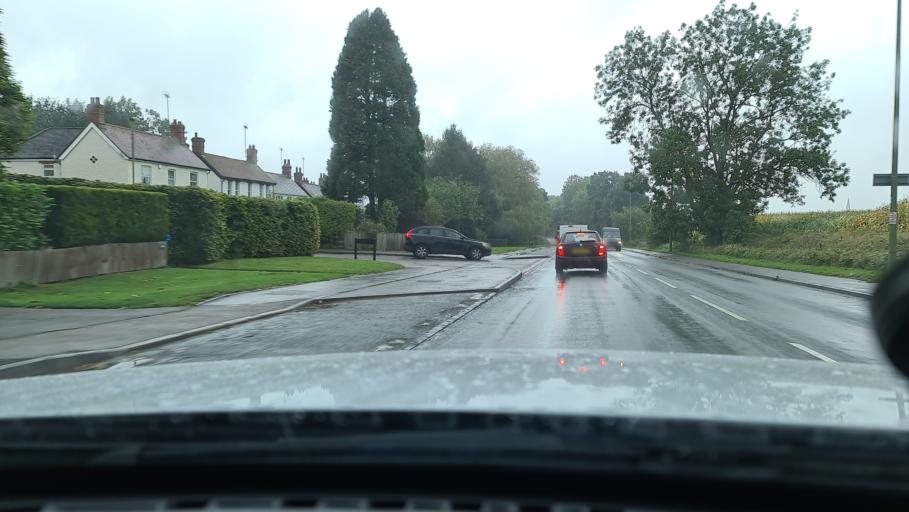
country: GB
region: England
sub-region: Oxfordshire
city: Adderbury
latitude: 52.0231
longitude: -1.3117
